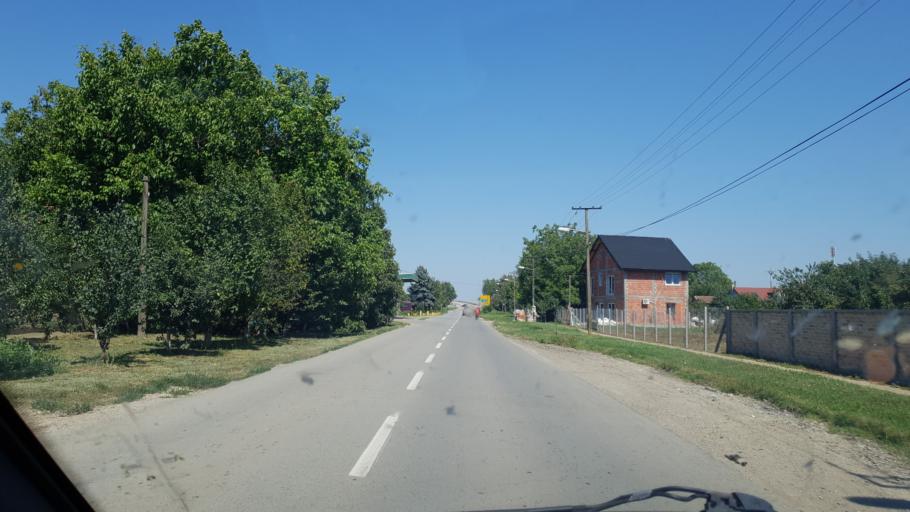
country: RS
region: Autonomna Pokrajina Vojvodina
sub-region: Juznobacki Okrug
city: Kovilj
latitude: 45.2379
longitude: 20.0319
